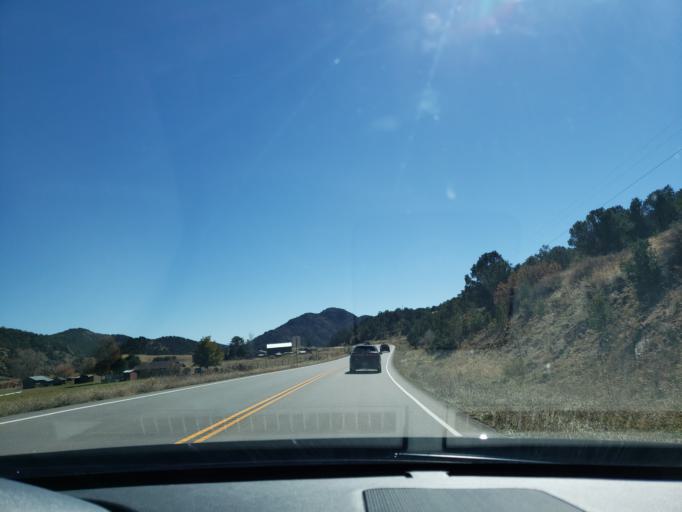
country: US
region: Colorado
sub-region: Fremont County
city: Canon City
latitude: 38.5986
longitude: -105.4280
